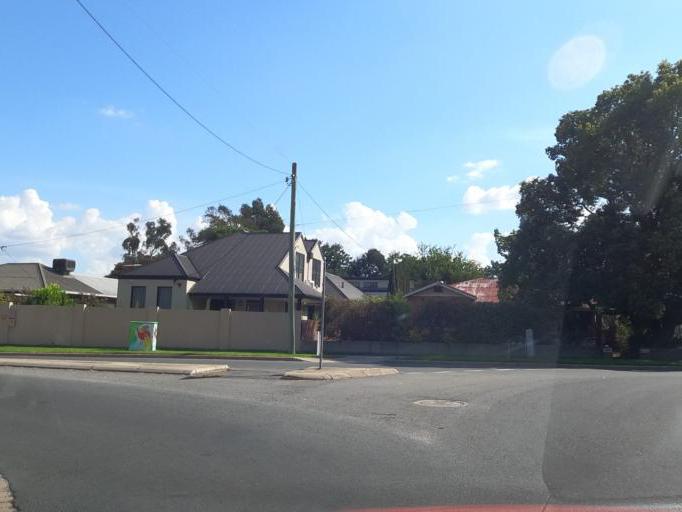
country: AU
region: New South Wales
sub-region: Albury Municipality
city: Albury
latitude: -36.0716
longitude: 146.9174
